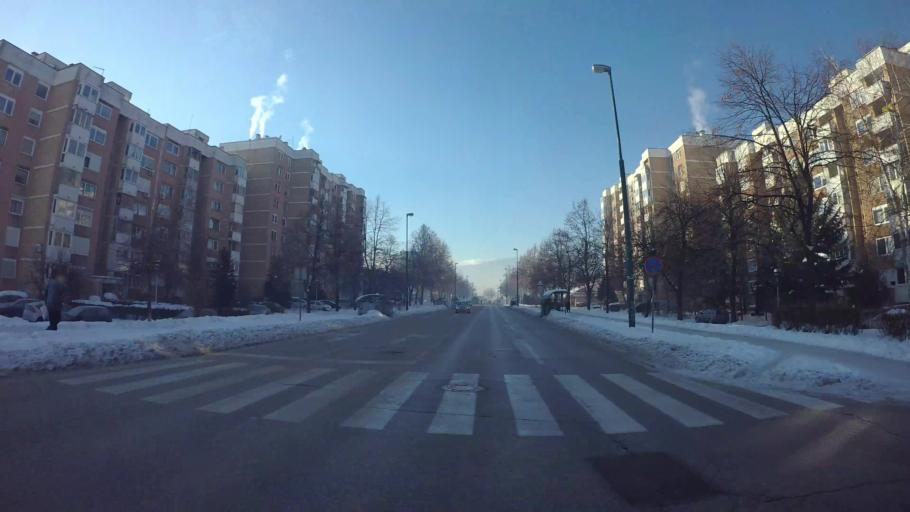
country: BA
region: Federation of Bosnia and Herzegovina
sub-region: Kanton Sarajevo
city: Sarajevo
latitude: 43.8291
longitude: 18.3501
